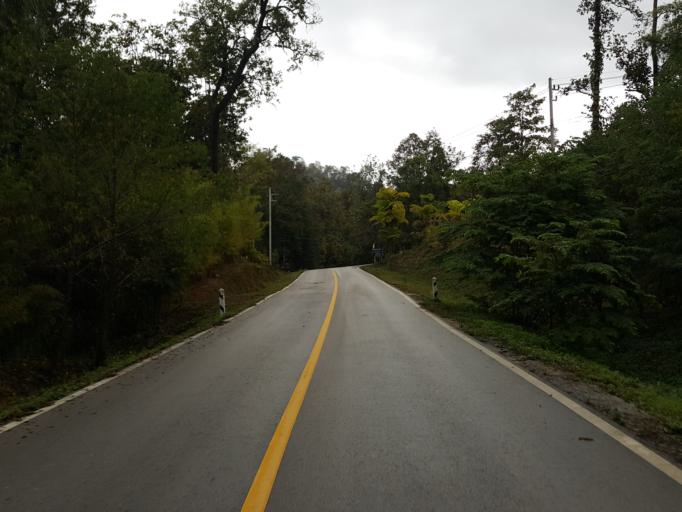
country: TH
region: Lampang
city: Hang Chat
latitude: 18.3575
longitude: 99.2456
